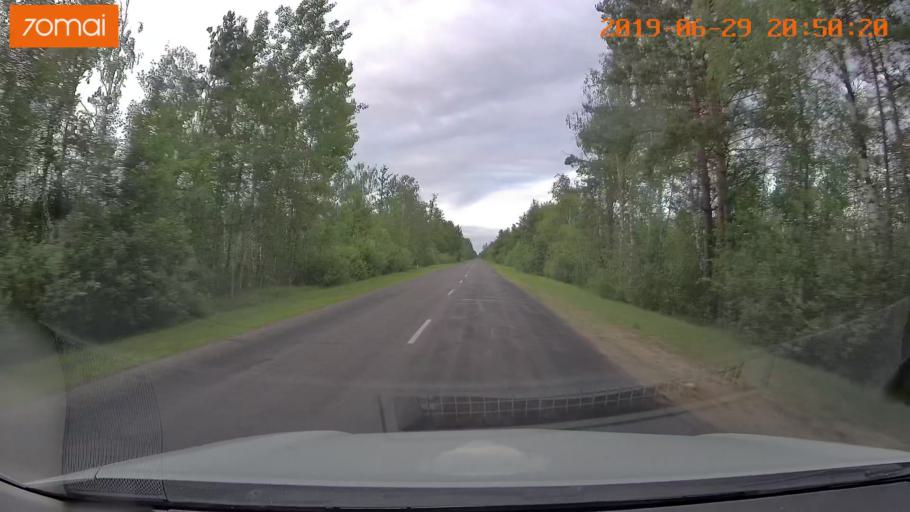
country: BY
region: Brest
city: Hantsavichy
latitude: 52.6753
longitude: 26.3344
